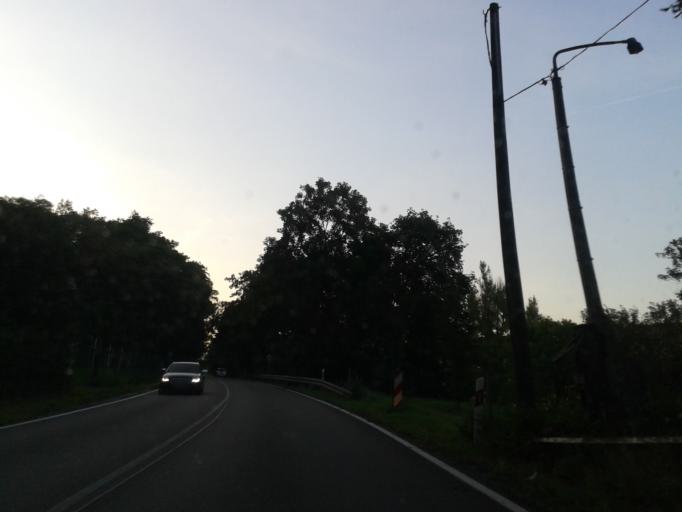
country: DE
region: Saxony
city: Meissen
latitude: 51.1795
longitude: 13.4549
